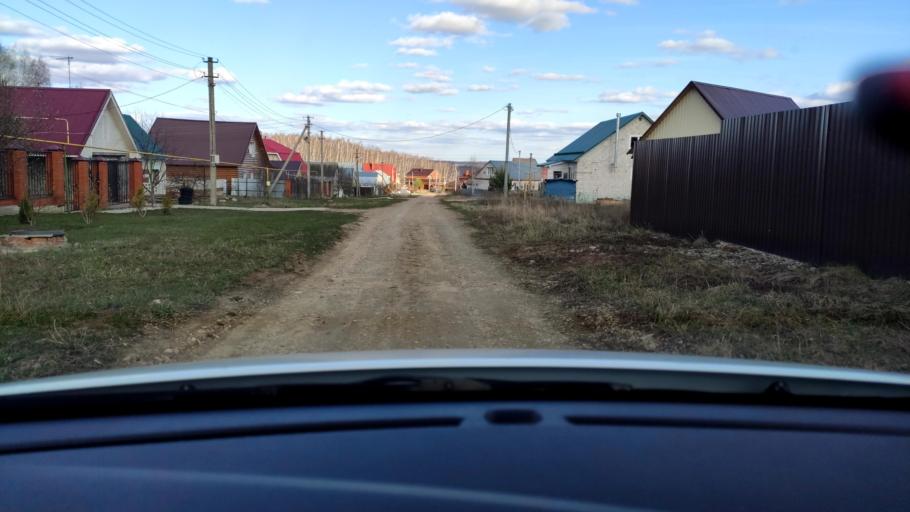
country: RU
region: Tatarstan
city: Vysokaya Gora
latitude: 55.8916
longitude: 49.3591
